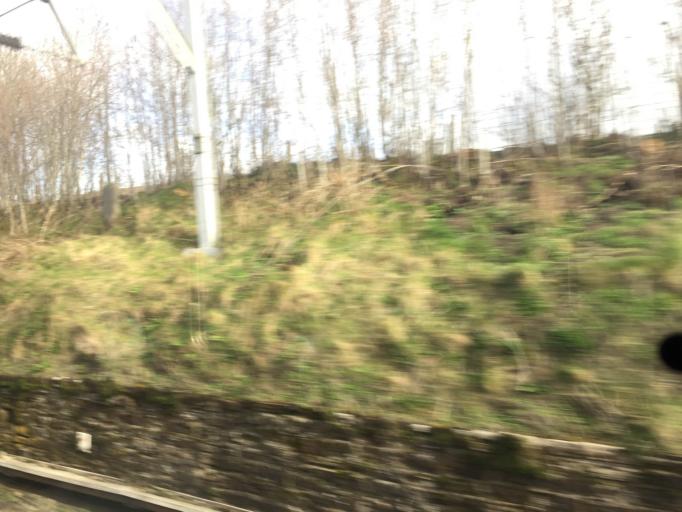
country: GB
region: England
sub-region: Cumbria
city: Penrith
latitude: 54.6412
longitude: -2.7574
